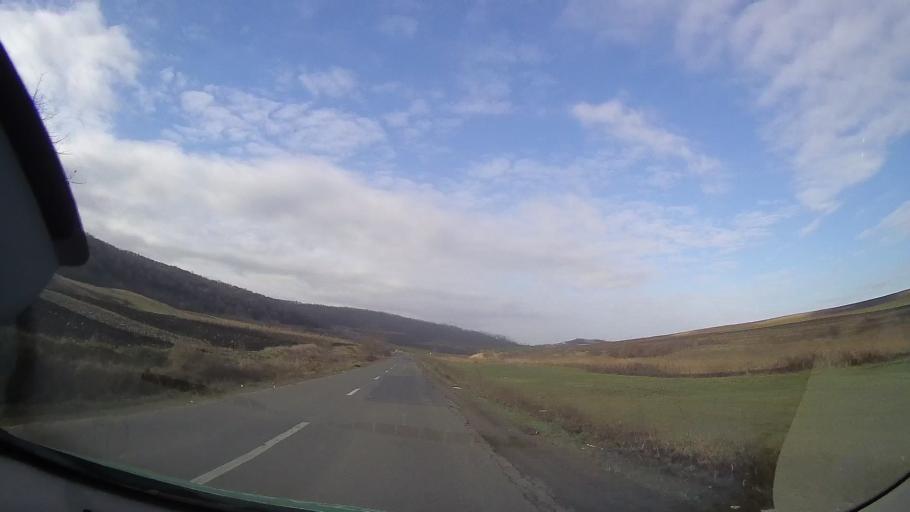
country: RO
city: Barza
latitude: 46.5535
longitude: 24.1065
